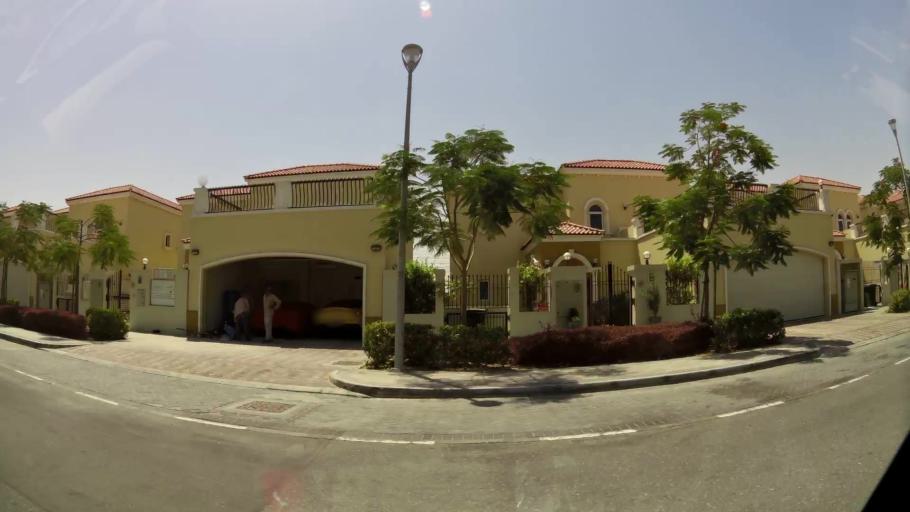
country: AE
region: Dubai
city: Dubai
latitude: 25.0376
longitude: 55.1693
